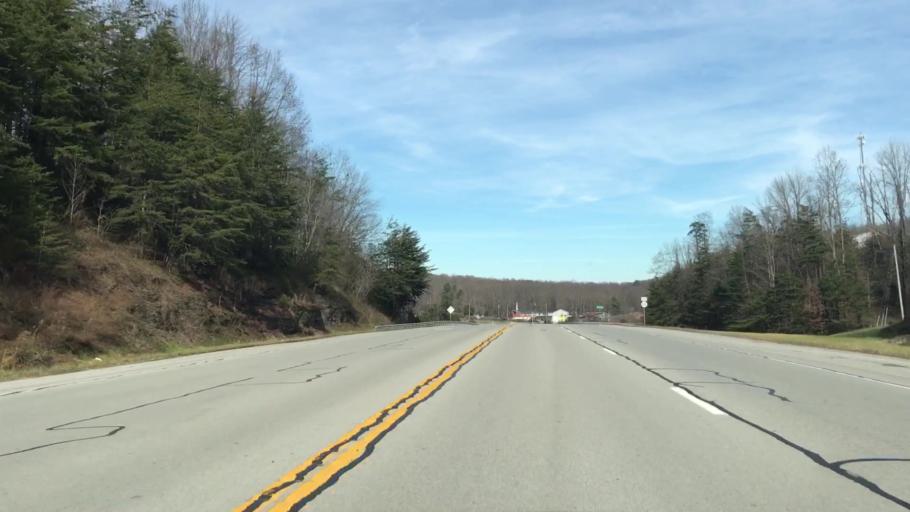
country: US
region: Kentucky
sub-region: McCreary County
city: Whitley City
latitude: 36.8361
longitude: -84.4823
